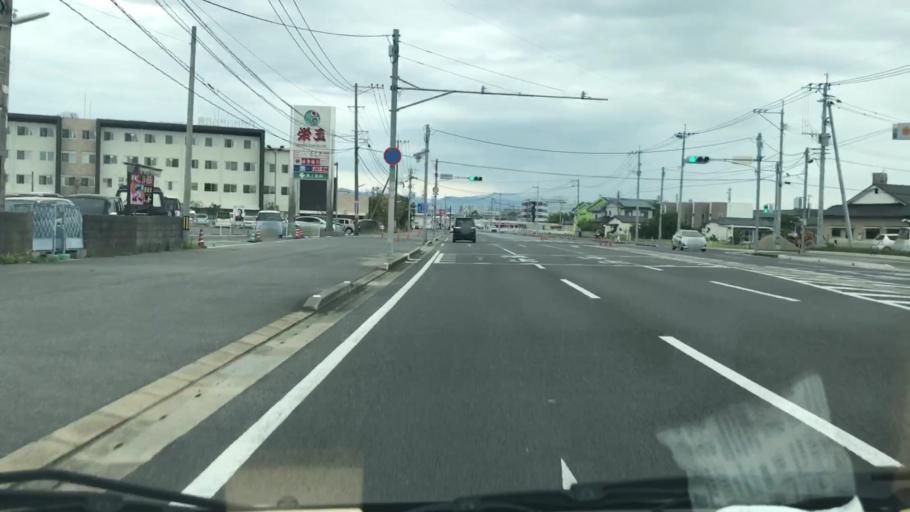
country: JP
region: Saga Prefecture
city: Saga-shi
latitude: 33.2361
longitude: 130.2938
